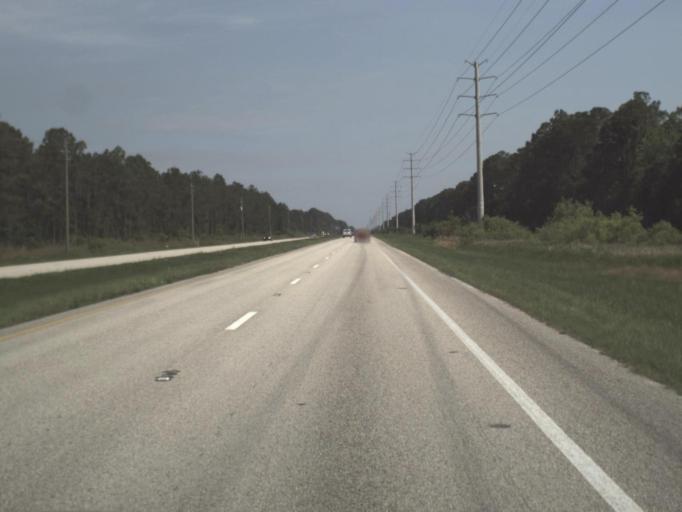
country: US
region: Florida
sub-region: Saint Johns County
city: Villano Beach
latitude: 30.0273
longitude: -81.4056
